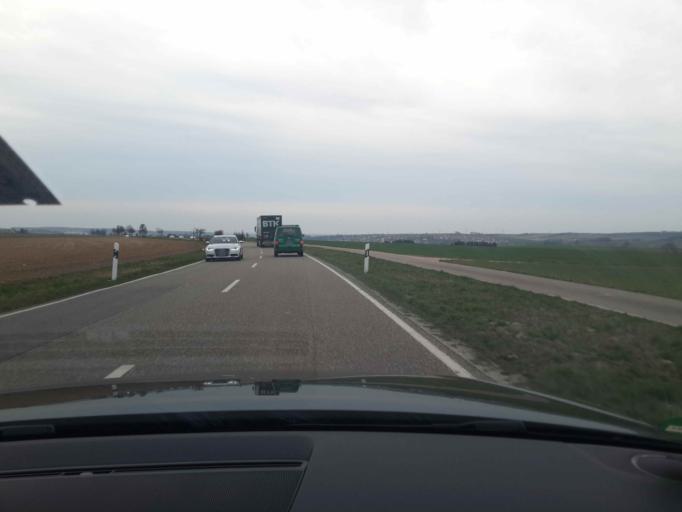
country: DE
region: Baden-Wuerttemberg
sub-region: Regierungsbezirk Stuttgart
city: Bretzfeld
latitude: 49.2311
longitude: 9.3996
